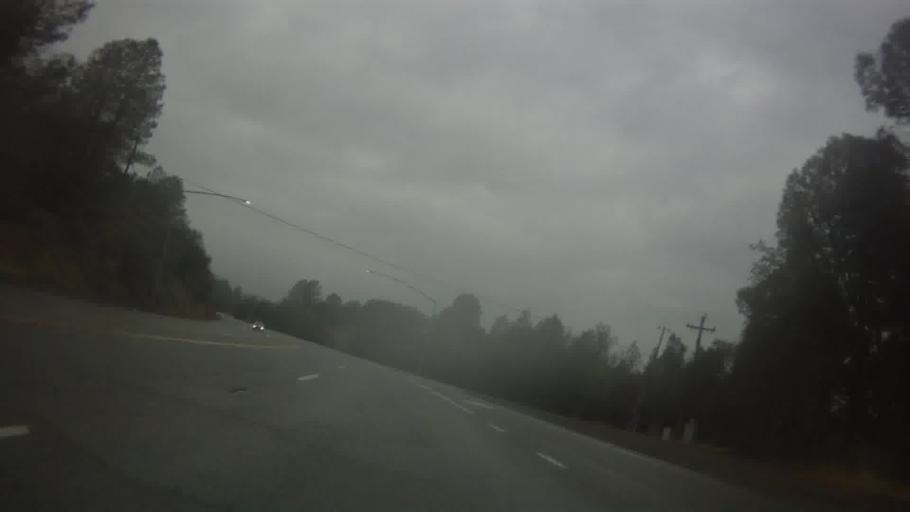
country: US
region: California
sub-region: Shasta County
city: Shasta
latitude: 40.5899
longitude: -122.4603
